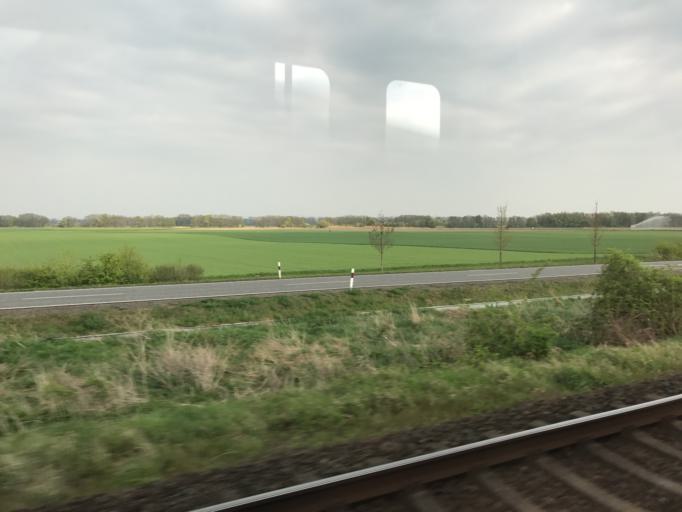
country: DE
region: Rheinland-Pfalz
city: Ludwigshohe
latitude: 49.8097
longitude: 8.3522
